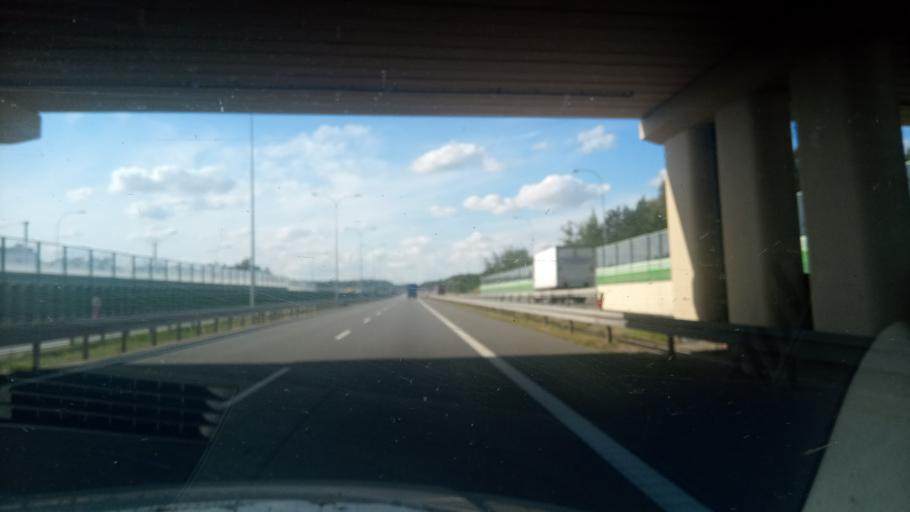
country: PL
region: Kujawsko-Pomorskie
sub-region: Powiat bydgoski
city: Biale Blota
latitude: 53.0885
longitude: 17.9027
